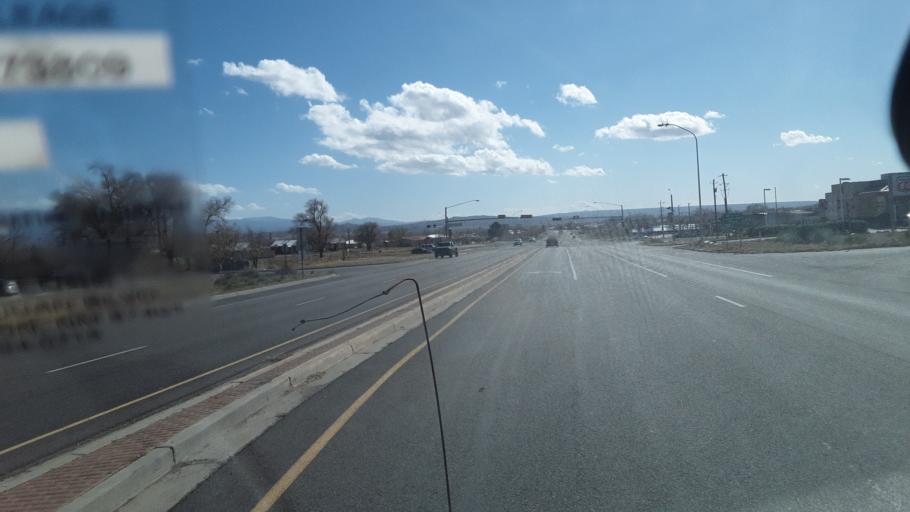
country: US
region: New Mexico
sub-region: Rio Arriba County
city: Espanola
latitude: 36.0095
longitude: -106.0882
